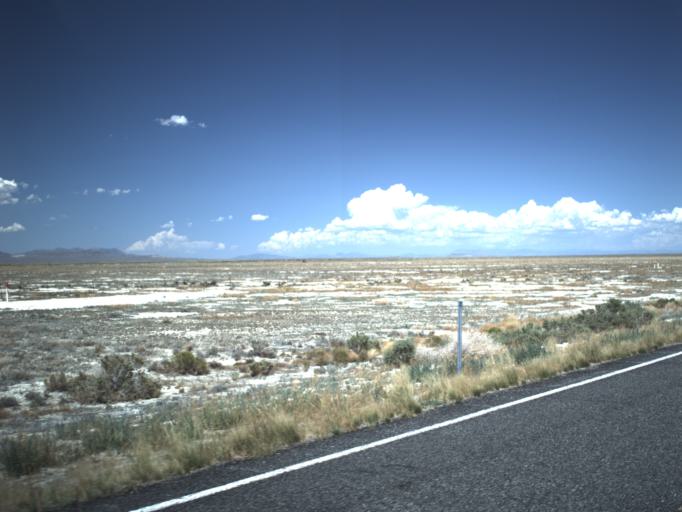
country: US
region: Utah
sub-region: Millard County
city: Delta
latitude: 39.2003
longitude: -112.9833
